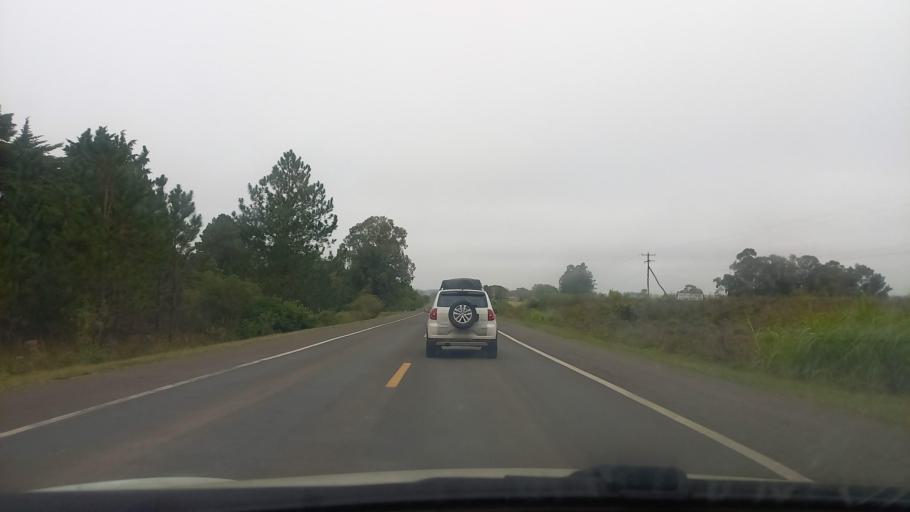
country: BR
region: Rio Grande do Sul
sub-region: Rosario Do Sul
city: Rosario do Sul
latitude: -30.2733
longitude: -54.9774
